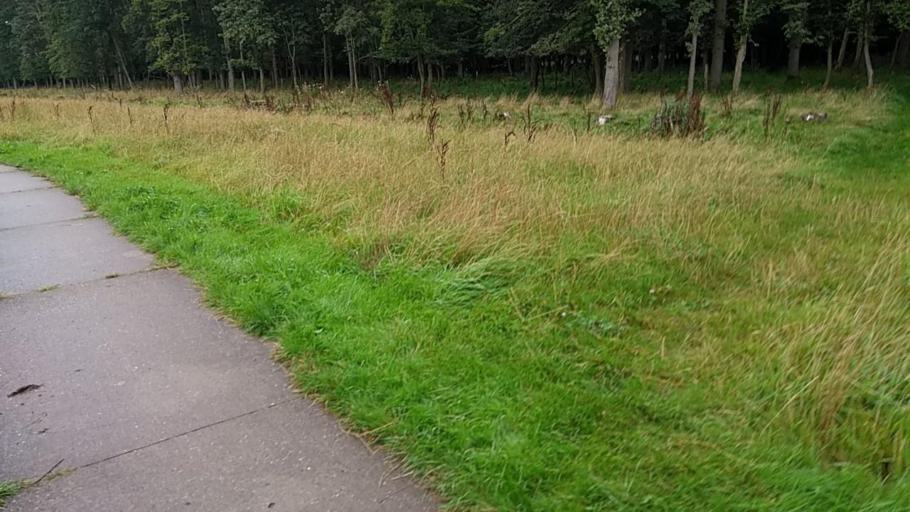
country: NL
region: Overijssel
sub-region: Gemeente Steenwijkerland
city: Vollenhove
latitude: 52.6650
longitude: 5.9347
